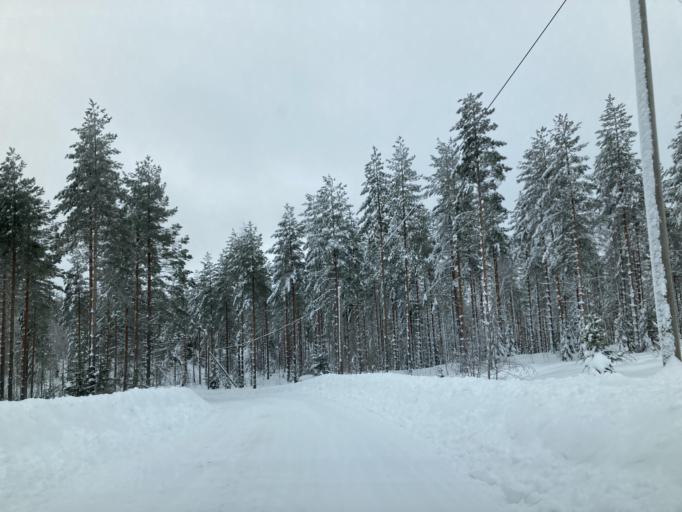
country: FI
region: Central Finland
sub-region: Jaemsae
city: Jaemsae
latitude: 61.8815
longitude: 25.3228
